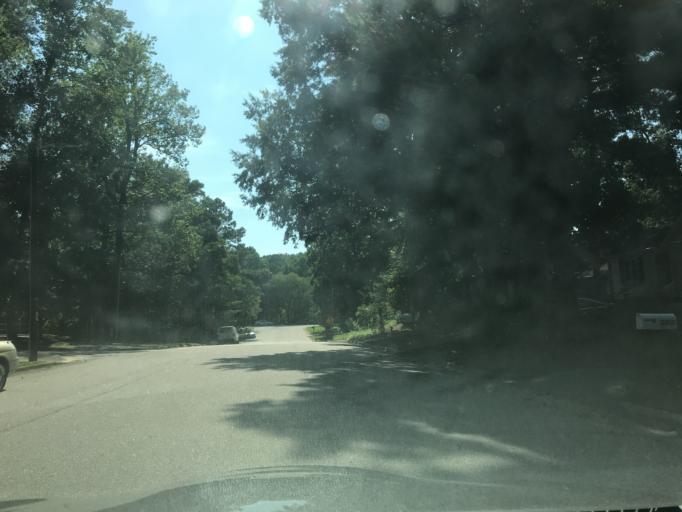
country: US
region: North Carolina
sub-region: Wake County
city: Raleigh
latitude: 35.8576
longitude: -78.6053
